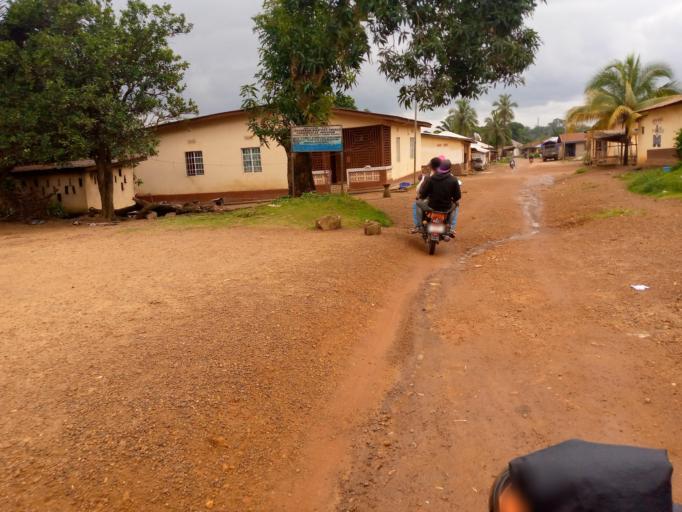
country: SL
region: Eastern Province
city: Kenema
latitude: 7.8700
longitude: -11.1824
